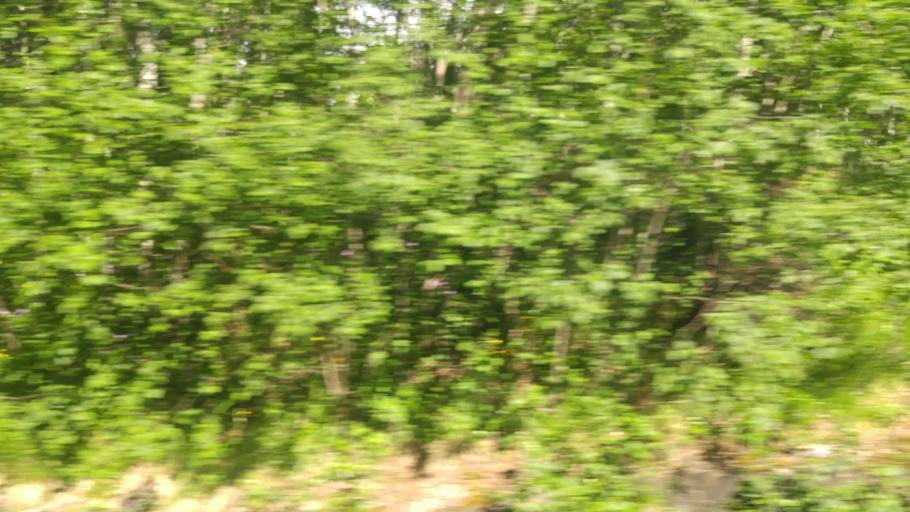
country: SE
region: Jaemtland
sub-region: Are Kommun
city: Are
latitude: 63.3895
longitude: 12.9062
